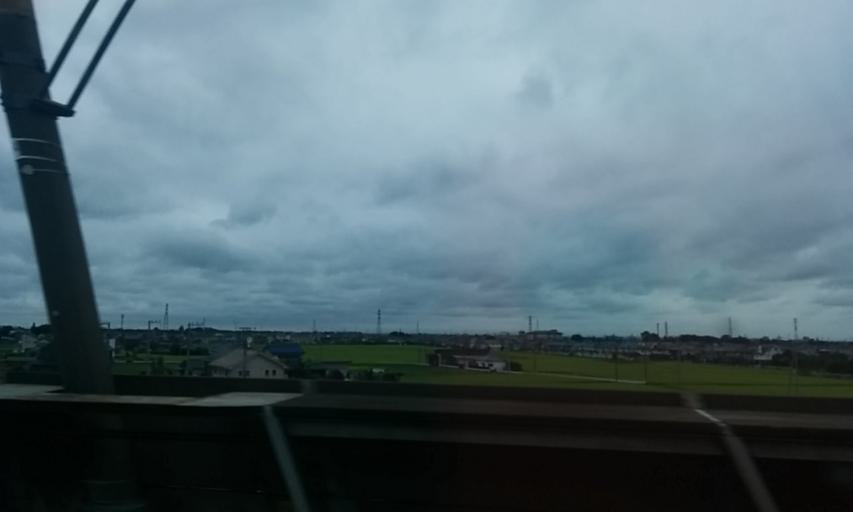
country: JP
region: Saitama
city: Kukichuo
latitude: 36.0904
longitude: 139.6933
